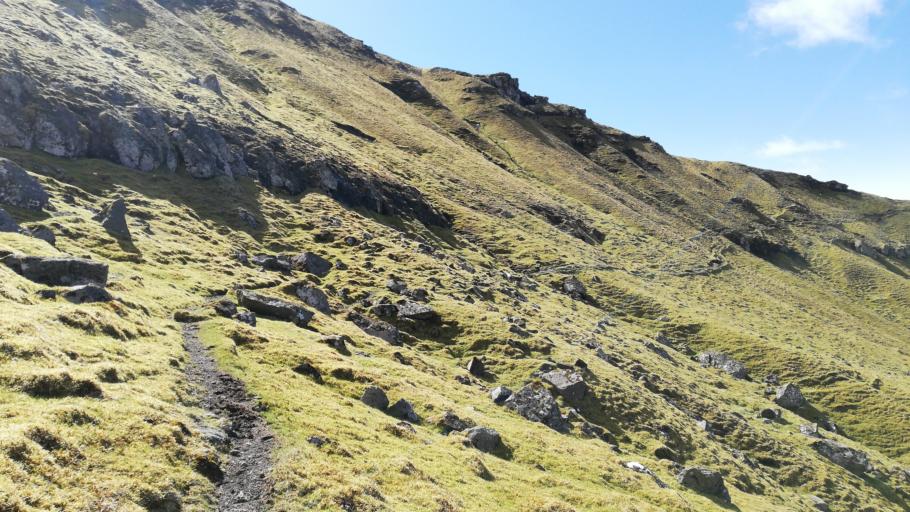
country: FO
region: Streymoy
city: Kollafjordhur
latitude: 62.0692
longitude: -6.9761
